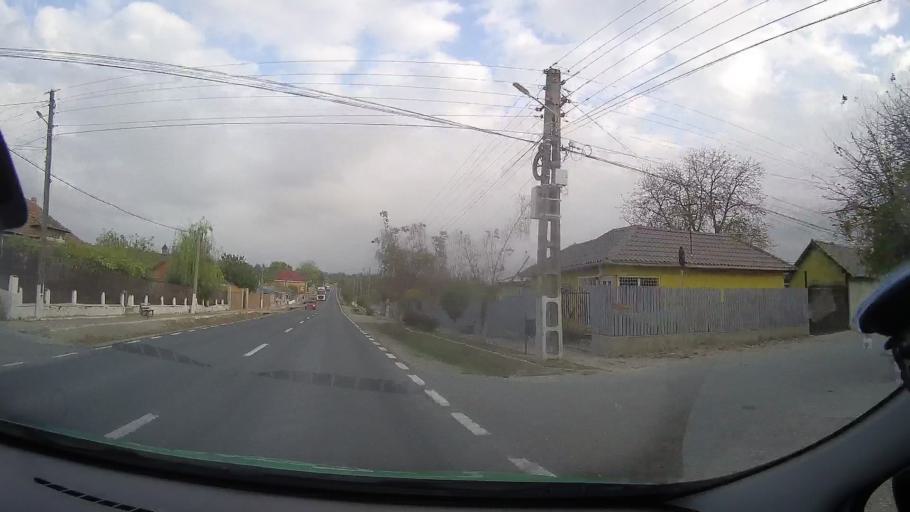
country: RO
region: Constanta
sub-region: Comuna Mircea Voda
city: Satu Nou
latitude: 44.2685
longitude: 28.2217
